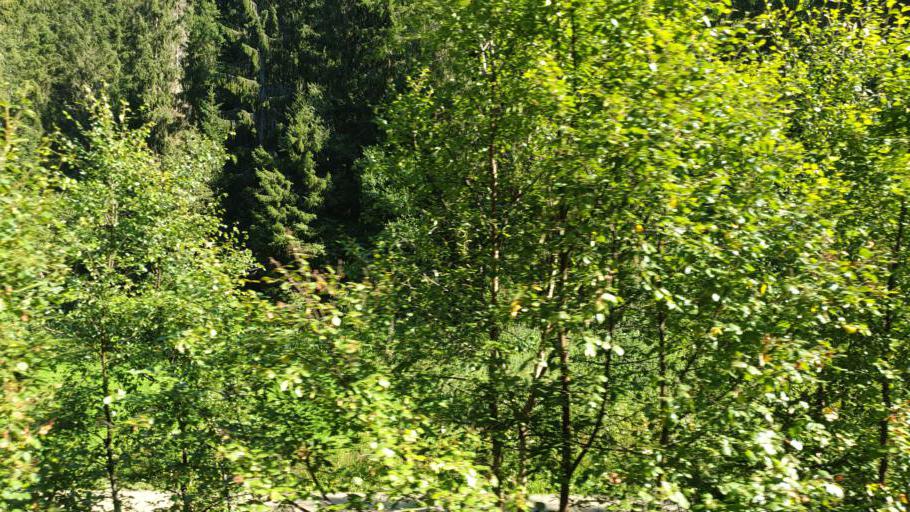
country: NO
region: Sor-Trondelag
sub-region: Orkdal
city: Orkanger
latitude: 63.1915
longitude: 9.7820
